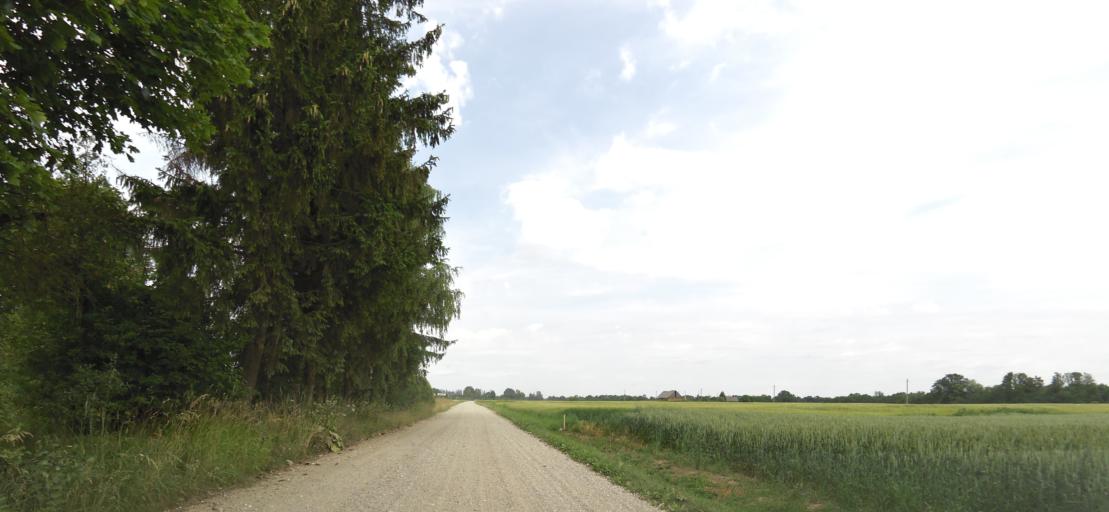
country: LT
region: Panevezys
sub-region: Birzai
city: Birzai
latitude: 56.3505
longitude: 24.7472
